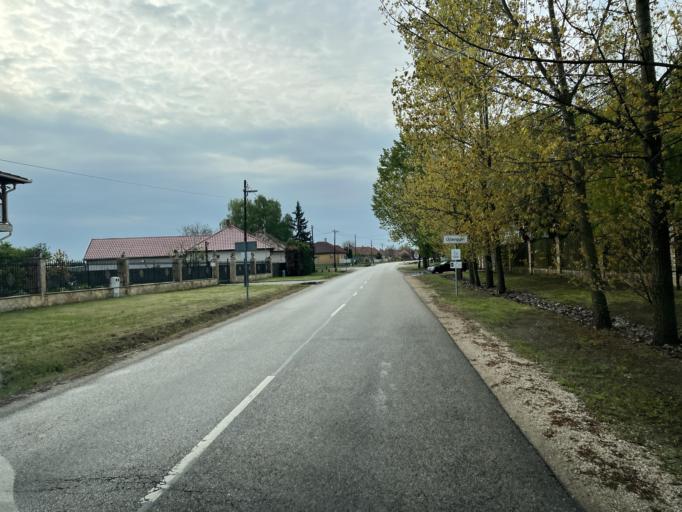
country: HU
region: Pest
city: Ujhartyan
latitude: 47.2362
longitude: 19.4448
